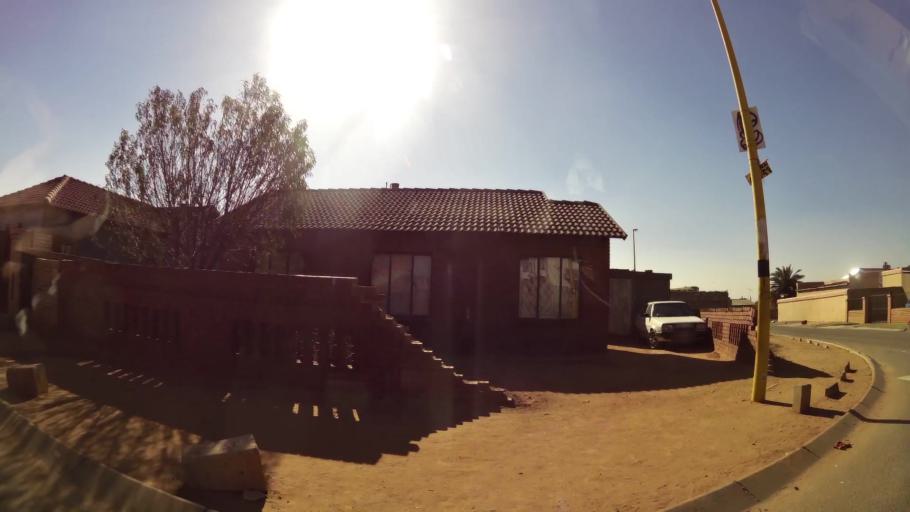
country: ZA
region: Gauteng
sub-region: Ekurhuleni Metropolitan Municipality
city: Tembisa
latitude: -26.0203
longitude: 28.2320
